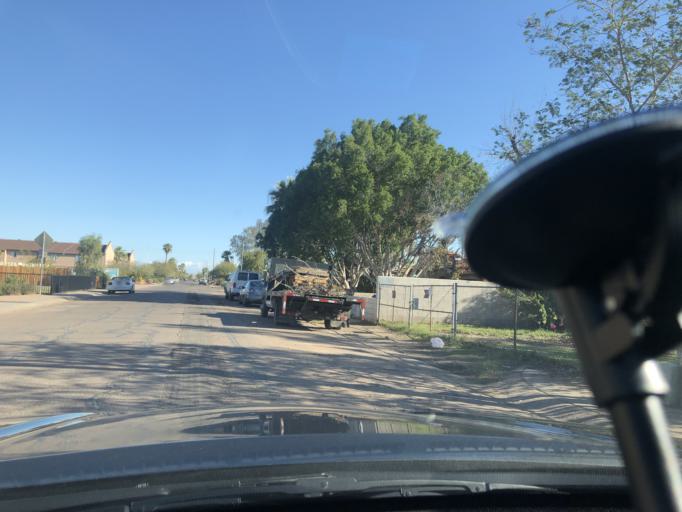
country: US
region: Arizona
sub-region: Maricopa County
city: Phoenix
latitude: 33.4712
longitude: -112.0465
